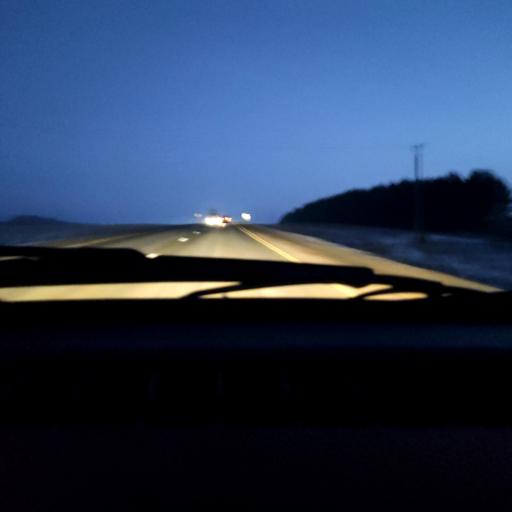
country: RU
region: Bashkortostan
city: Mikhaylovka
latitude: 54.7897
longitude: 55.7687
